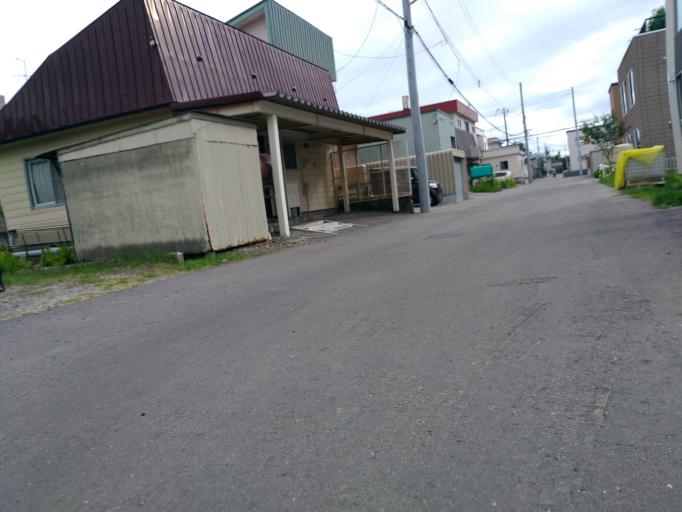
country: JP
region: Hokkaido
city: Ebetsu
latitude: 43.0863
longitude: 141.5268
